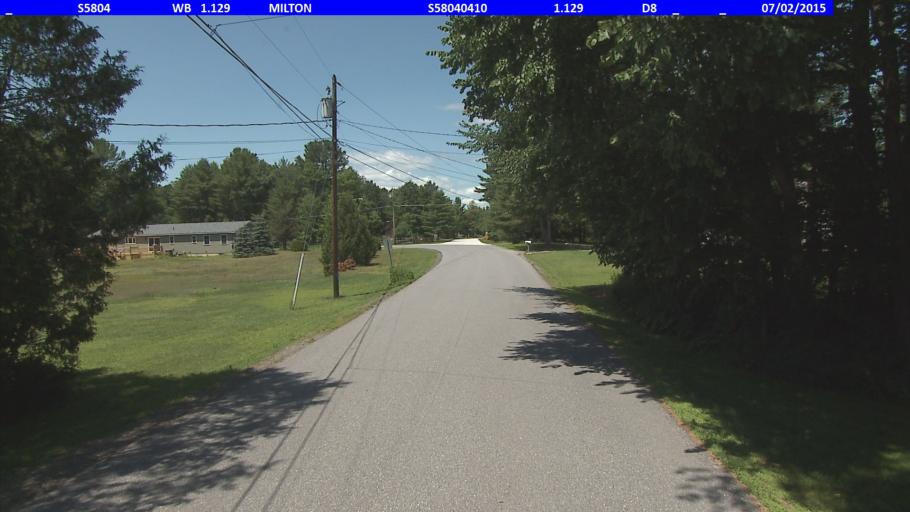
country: US
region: Vermont
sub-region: Chittenden County
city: Milton
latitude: 44.6571
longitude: -73.1515
